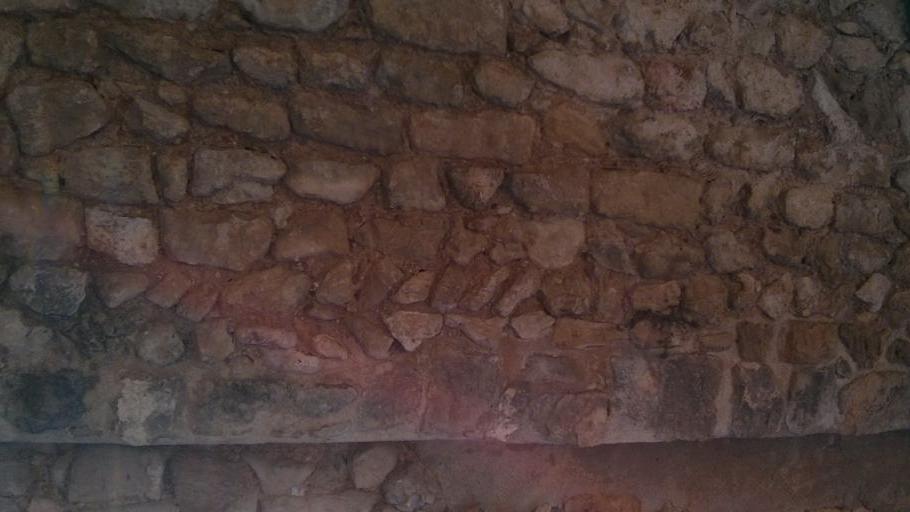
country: ES
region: Balearic Islands
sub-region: Illes Balears
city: Palma
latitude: 39.5703
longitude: 2.6417
